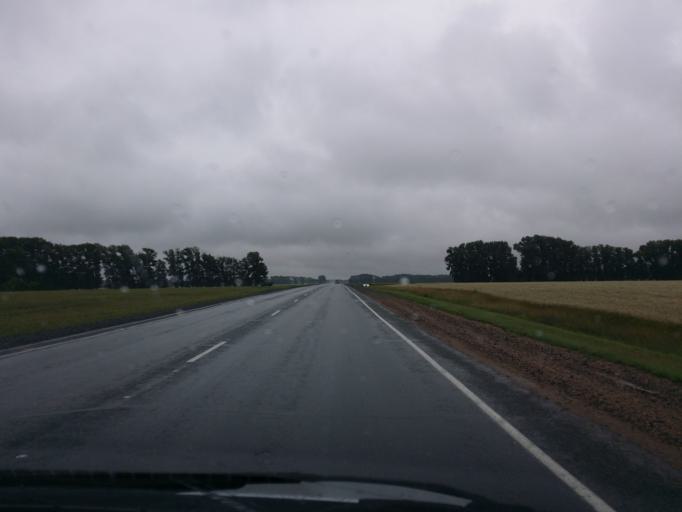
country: RU
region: Altai Krai
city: Bayunovskiye Klyuchi
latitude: 53.2863
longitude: 84.3317
